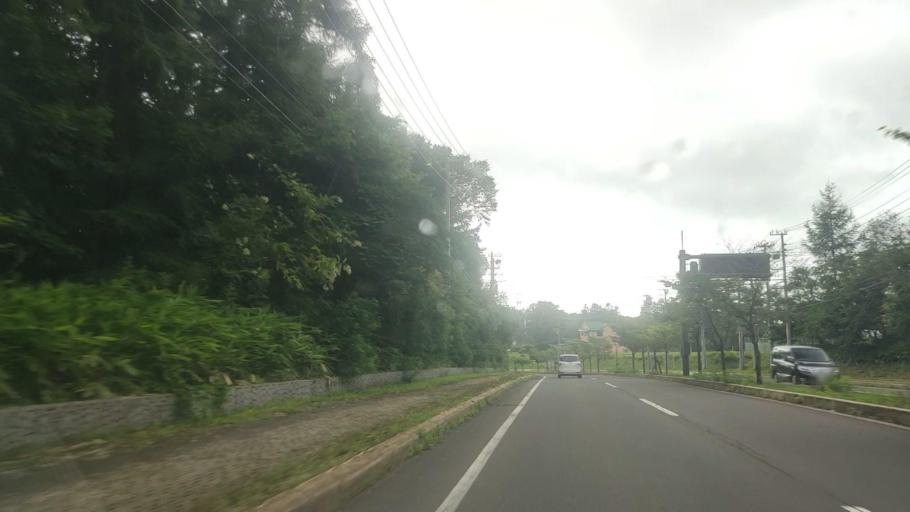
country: JP
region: Hokkaido
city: Shiraoi
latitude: 42.4730
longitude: 141.1479
